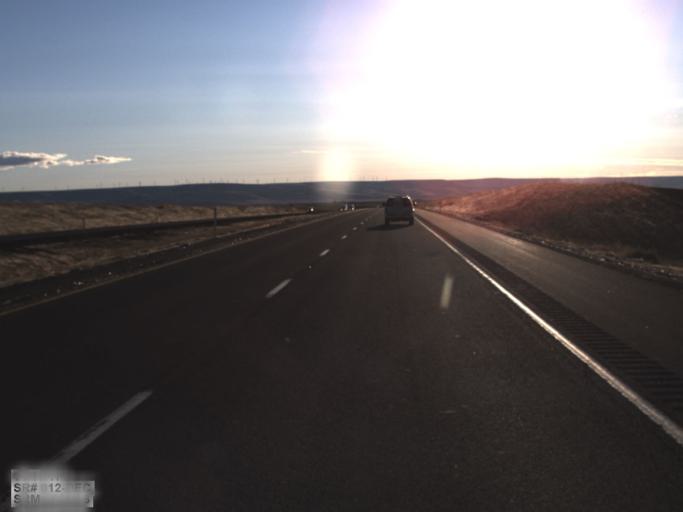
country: US
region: Washington
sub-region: Walla Walla County
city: Garrett
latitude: 46.0666
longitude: -118.4245
